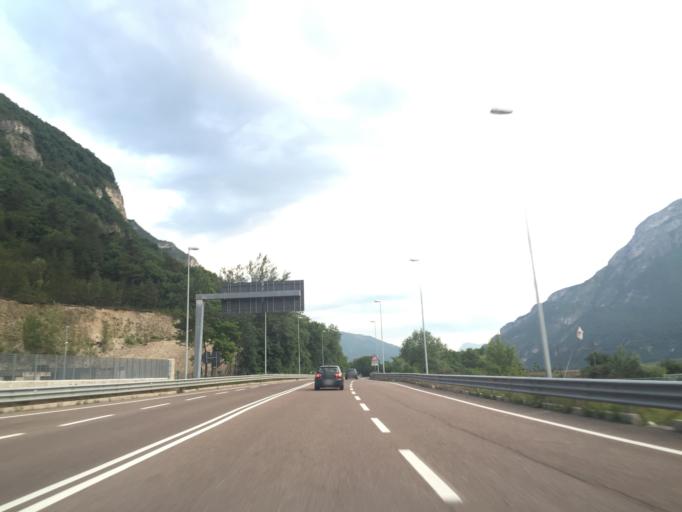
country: IT
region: Trentino-Alto Adige
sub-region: Provincia di Trento
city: Aldeno
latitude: 45.9786
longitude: 11.1147
